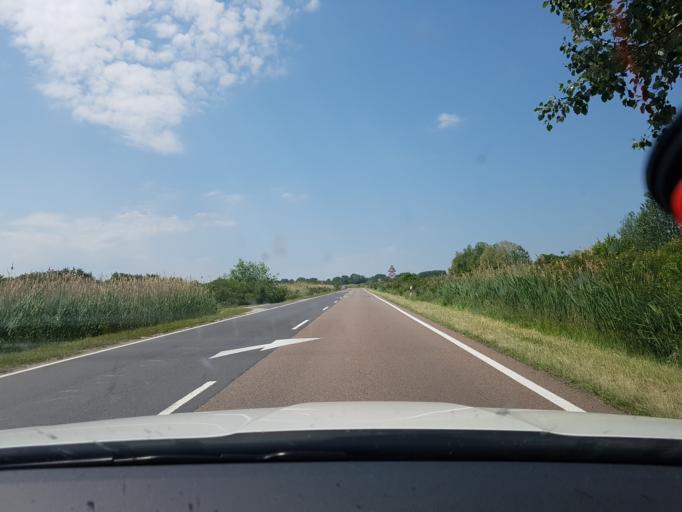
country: HU
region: Hajdu-Bihar
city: Tiszacsege
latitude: 47.5874
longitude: 21.0150
